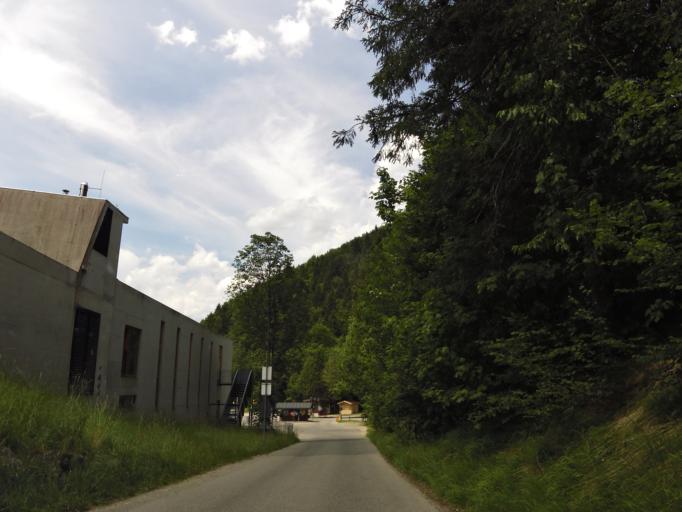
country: DE
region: Bavaria
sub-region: Upper Bavaria
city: Reit im Winkl
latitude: 47.6577
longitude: 12.5414
